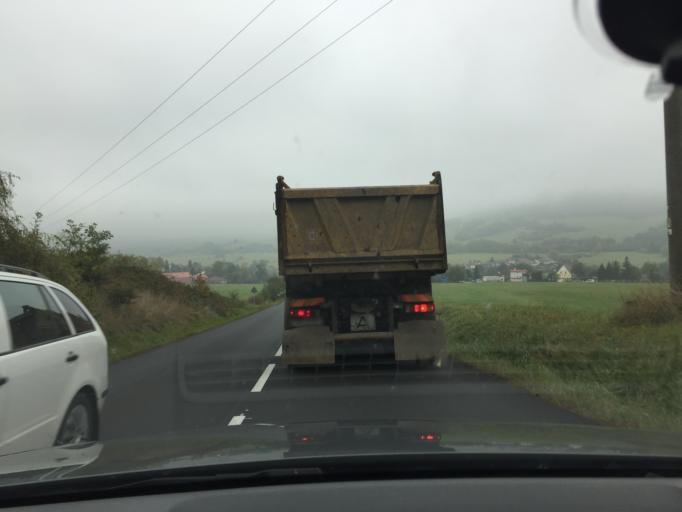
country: CZ
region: Ustecky
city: Libouchec
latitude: 50.7648
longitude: 14.0421
